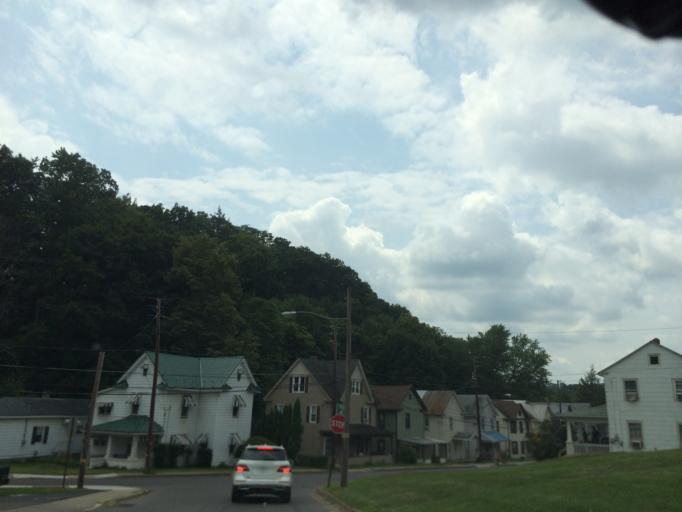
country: US
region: Pennsylvania
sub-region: Columbia County
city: Bloomsburg
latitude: 41.0067
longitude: -76.4579
